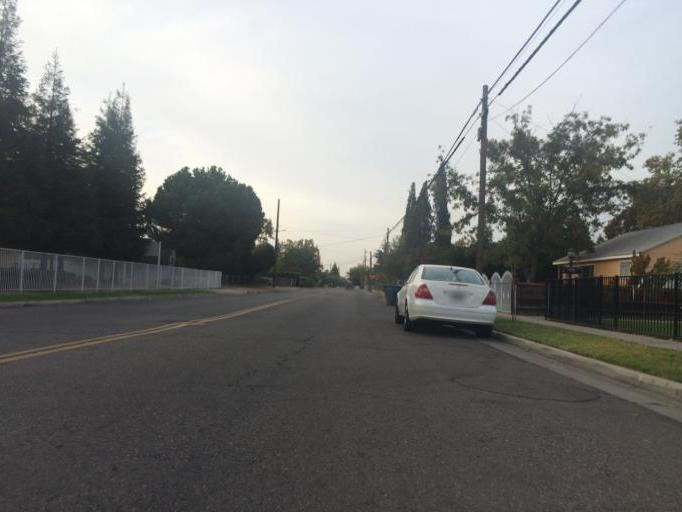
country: US
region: California
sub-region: Fresno County
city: Fresno
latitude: 36.7631
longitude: -119.7635
